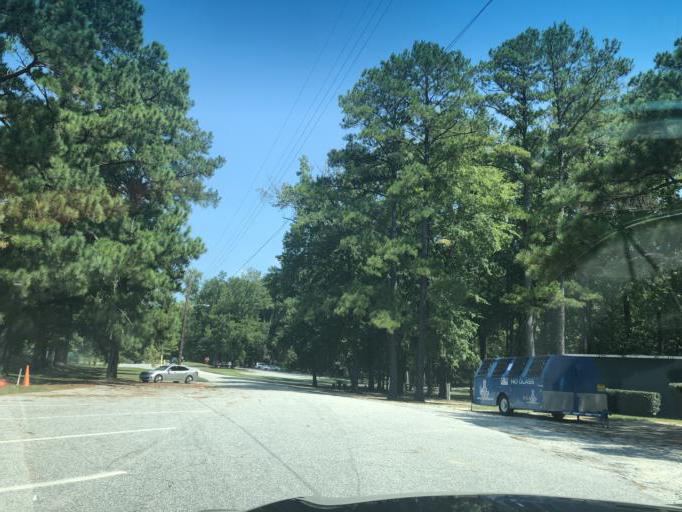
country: US
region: Georgia
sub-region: Muscogee County
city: Columbus
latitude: 32.5127
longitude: -84.9123
